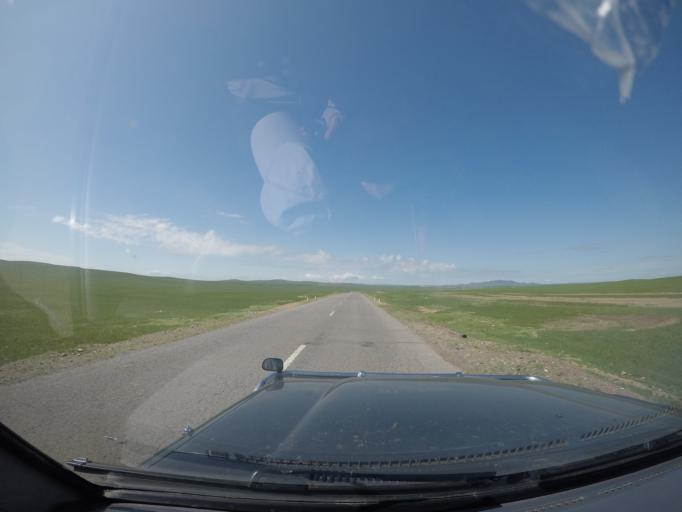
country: MN
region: Suhbaatar
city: Bayasgalant
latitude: 47.3435
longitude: 111.6126
